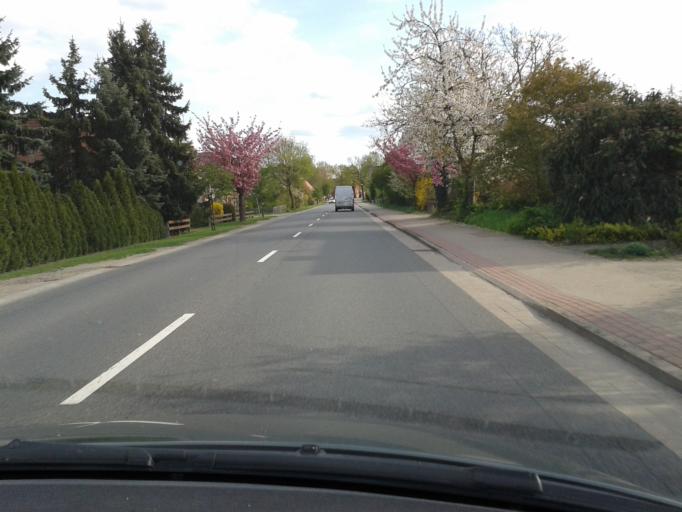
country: DE
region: Lower Saxony
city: Lubbow
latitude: 52.9115
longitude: 11.1811
